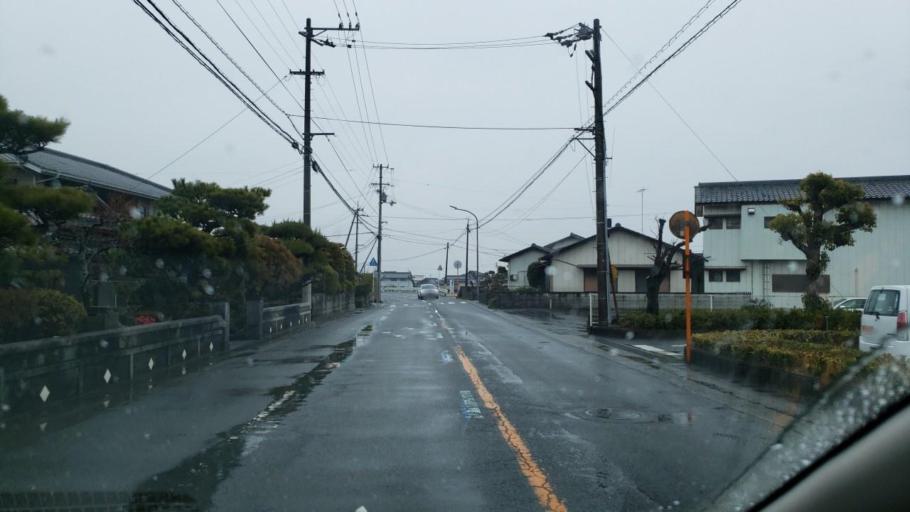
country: JP
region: Tokushima
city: Kamojimacho-jogejima
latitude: 34.0974
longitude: 134.3733
